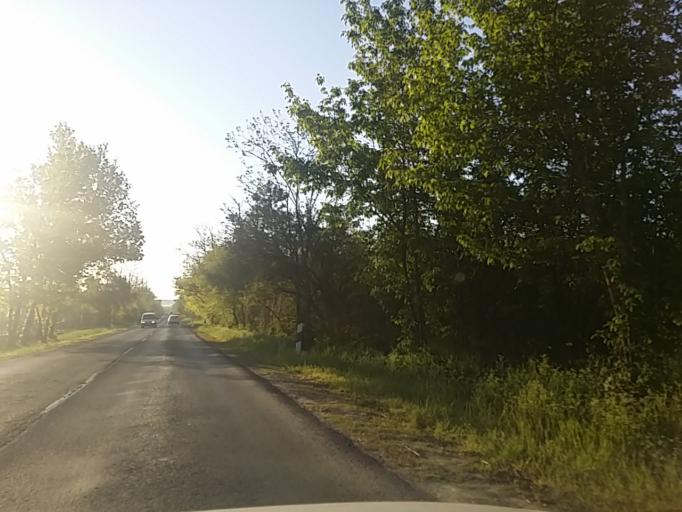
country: HU
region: Pest
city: Fot
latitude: 47.6031
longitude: 19.2084
